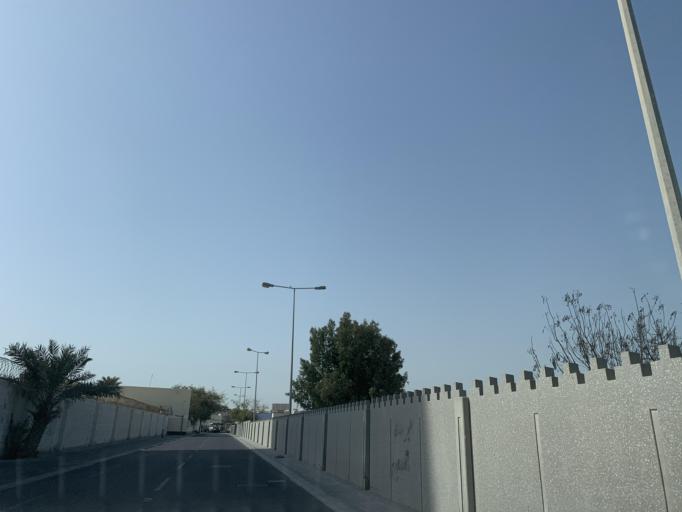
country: BH
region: Muharraq
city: Al Muharraq
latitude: 26.2664
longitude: 50.6141
